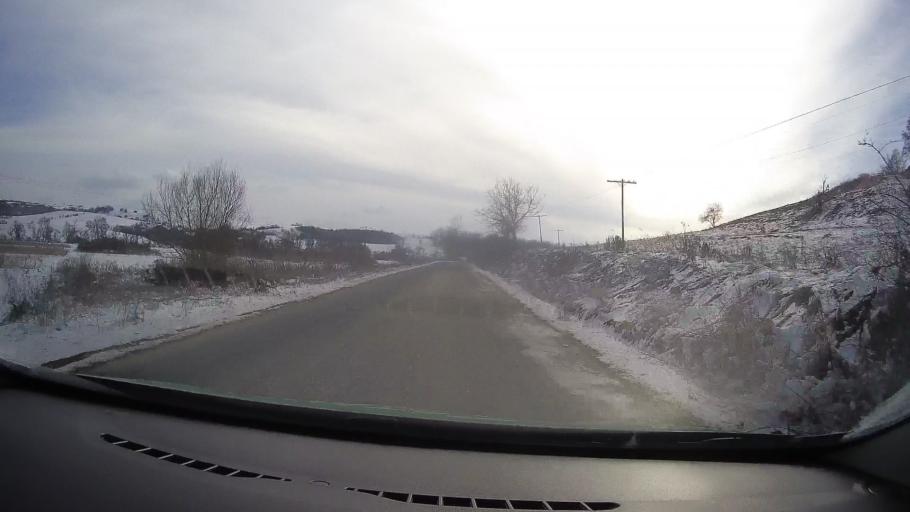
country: RO
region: Sibiu
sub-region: Comuna Iacobeni
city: Iacobeni
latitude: 46.0180
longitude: 24.6957
